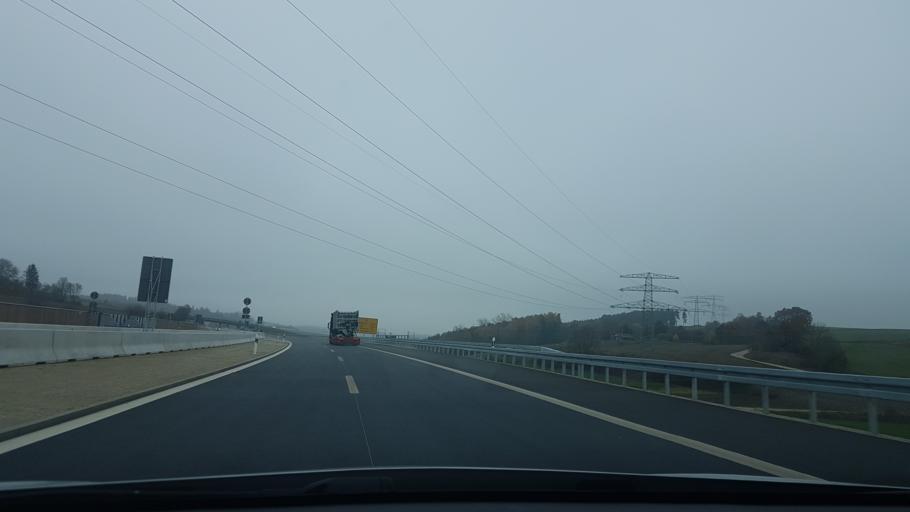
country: DE
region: Bavaria
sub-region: Lower Bavaria
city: Essenbach
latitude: 48.6218
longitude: 12.2254
